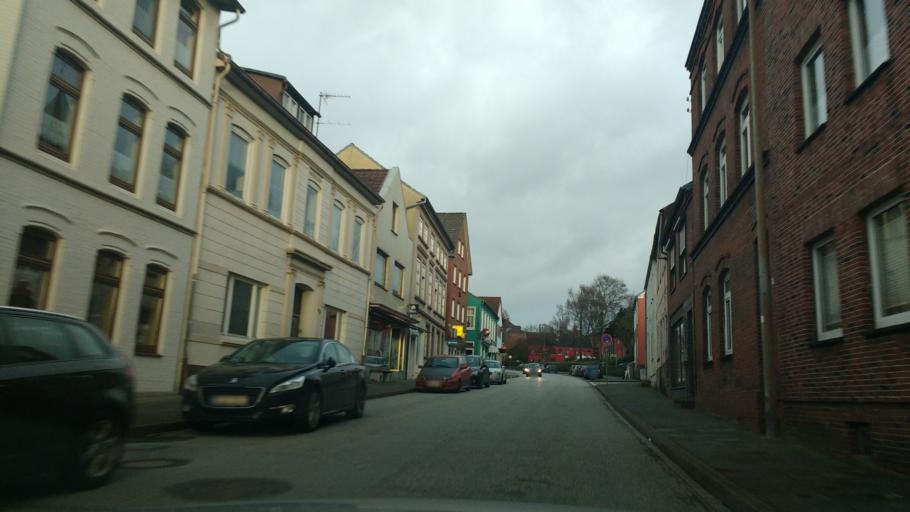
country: DE
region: Schleswig-Holstein
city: Itzehoe
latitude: 53.9249
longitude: 9.5231
